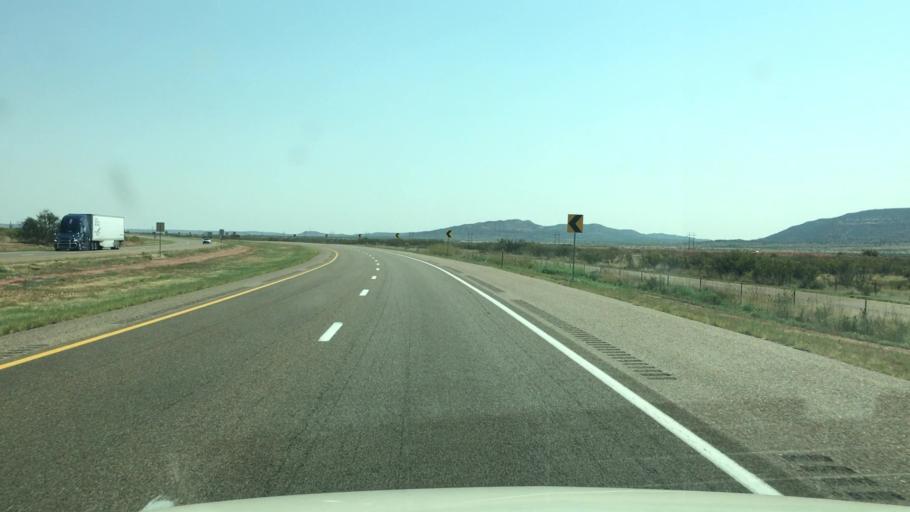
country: US
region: New Mexico
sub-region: Quay County
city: Tucumcari
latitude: 35.0936
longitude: -104.0641
